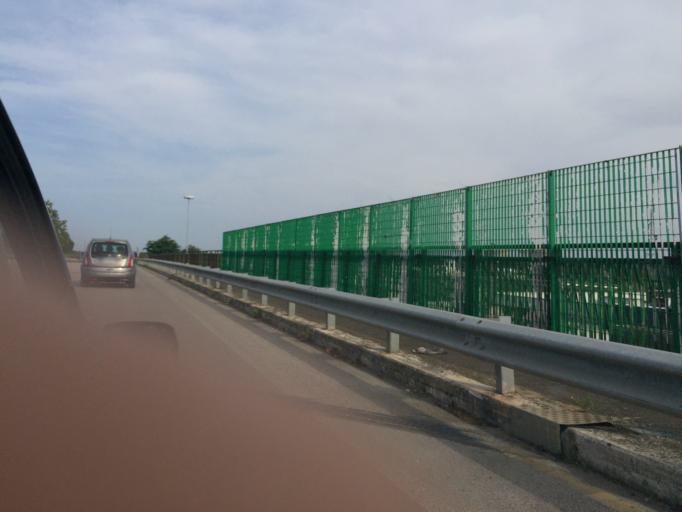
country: IT
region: Apulia
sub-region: Provincia di Bari
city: Triggiano
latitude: 41.1003
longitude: 16.9146
